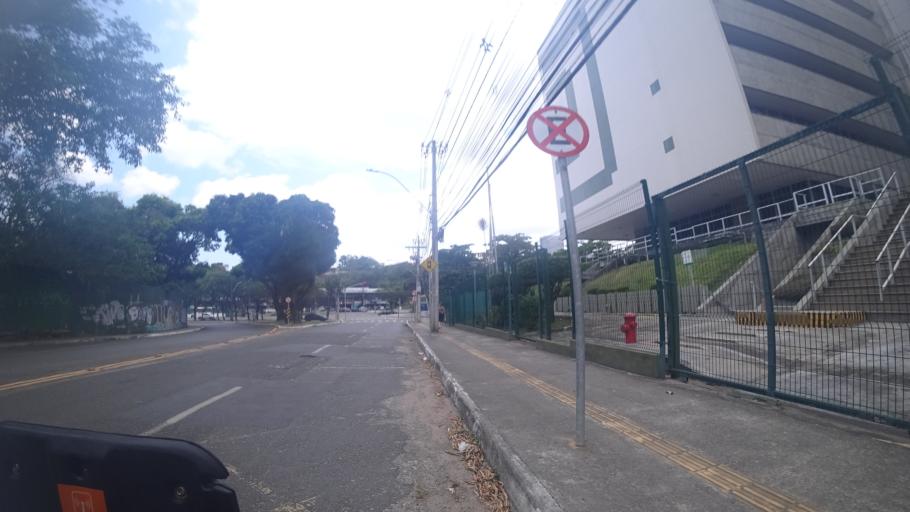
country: BR
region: Bahia
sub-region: Salvador
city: Salvador
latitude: -12.9971
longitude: -38.4689
